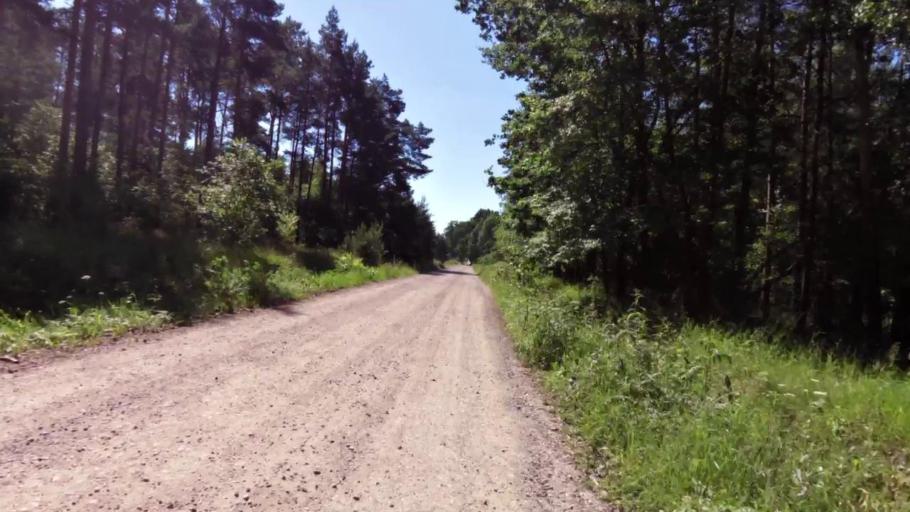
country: PL
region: West Pomeranian Voivodeship
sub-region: Powiat swidwinski
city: Rabino
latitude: 53.8964
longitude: 16.0092
